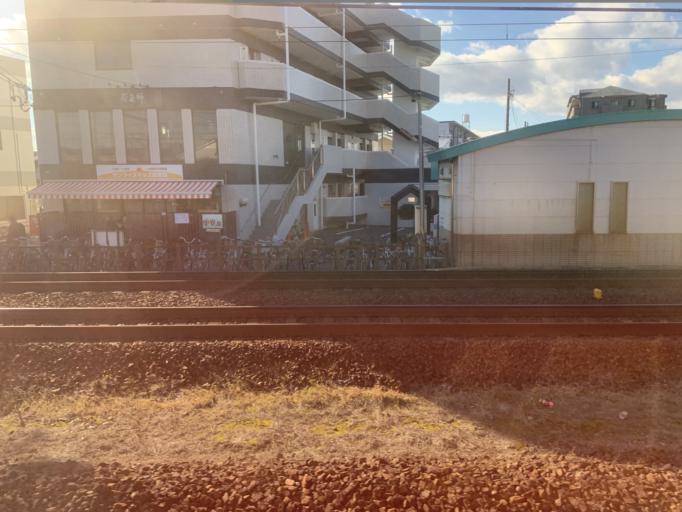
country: JP
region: Aichi
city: Ichinomiya
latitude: 35.3183
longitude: 136.7893
